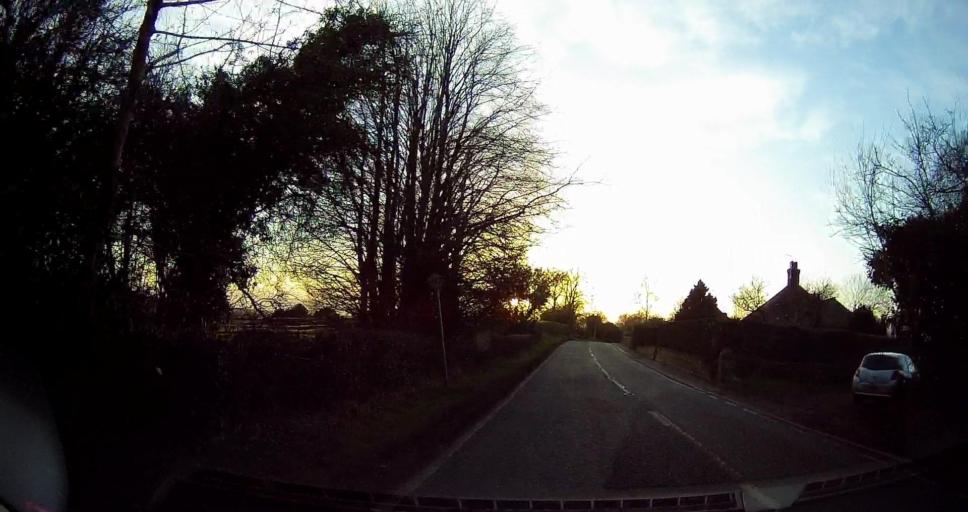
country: GB
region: England
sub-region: West Sussex
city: Maidenbower
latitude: 51.0952
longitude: -0.1126
